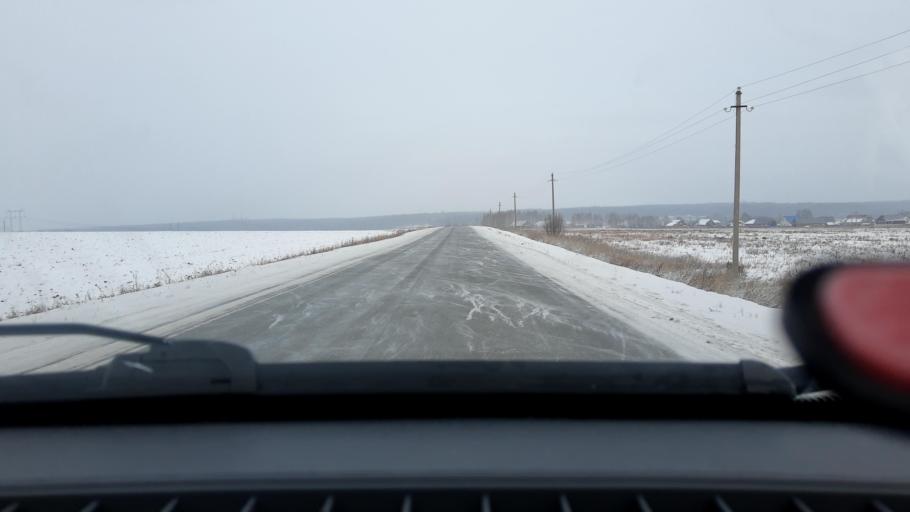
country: RU
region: Bashkortostan
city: Iglino
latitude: 54.7480
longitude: 56.3989
